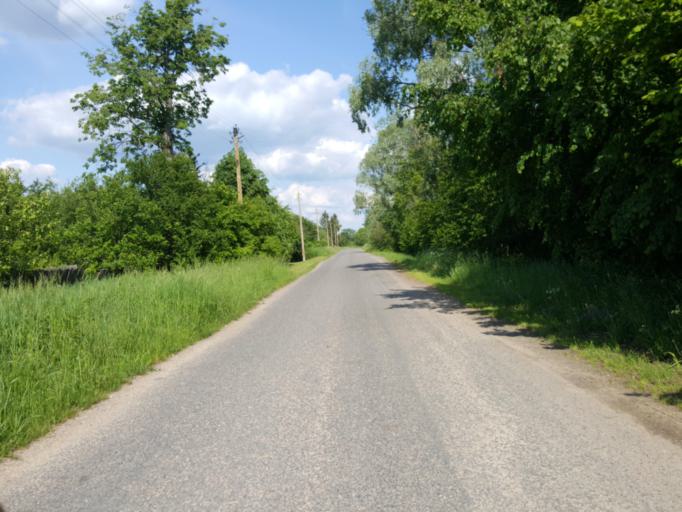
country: BY
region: Brest
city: Vysokaye
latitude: 52.4498
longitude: 23.5834
